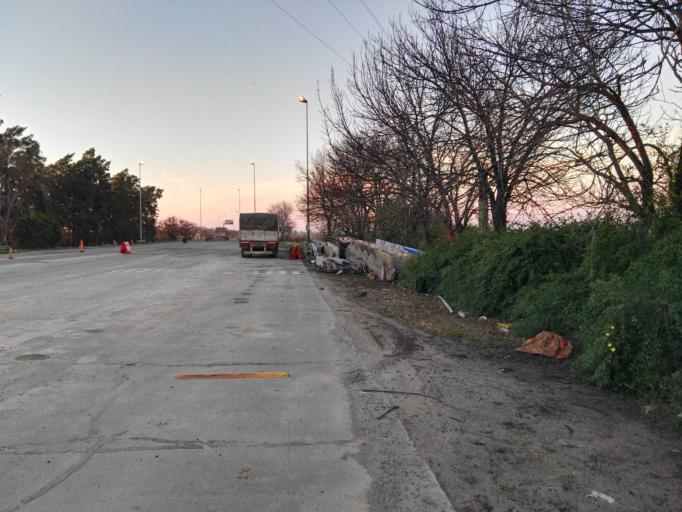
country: AR
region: Santa Fe
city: Laguna Paiva
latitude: -31.2906
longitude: -60.7580
